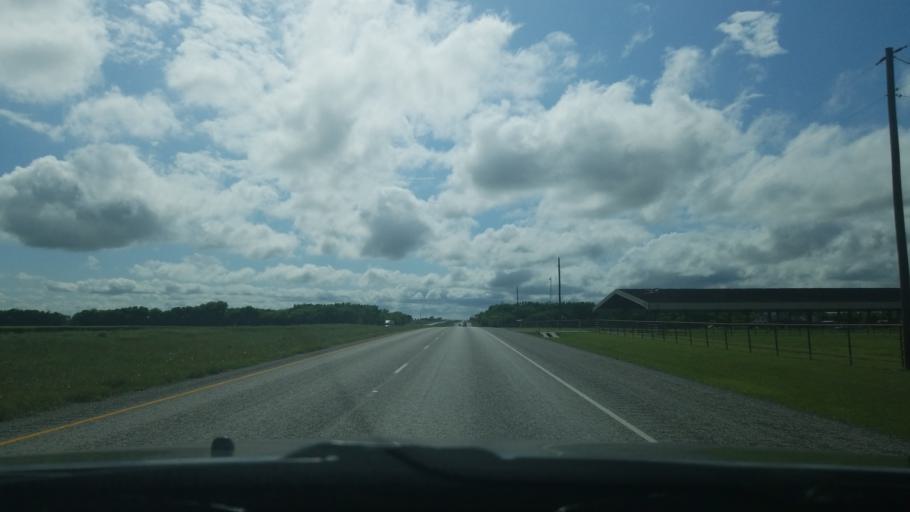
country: US
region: Texas
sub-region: Denton County
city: Ponder
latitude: 33.2383
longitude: -97.3126
